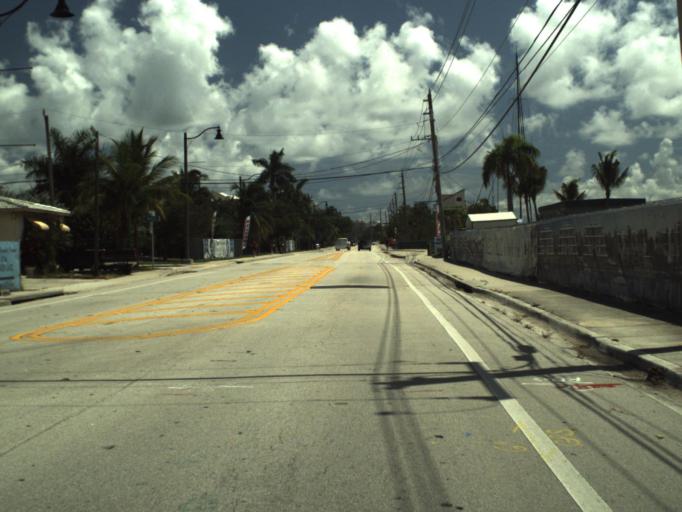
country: US
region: Florida
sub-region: Broward County
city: Dania Beach
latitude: 26.0514
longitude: -80.1145
